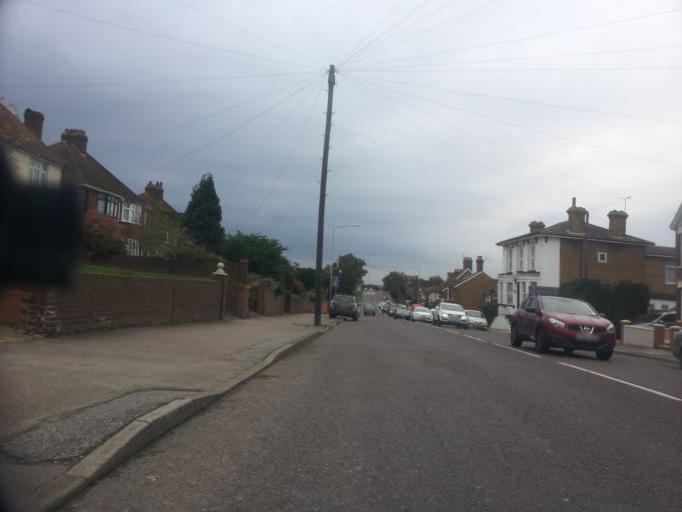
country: GB
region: England
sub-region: Kent
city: Sittingbourne
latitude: 51.3364
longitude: 0.7570
